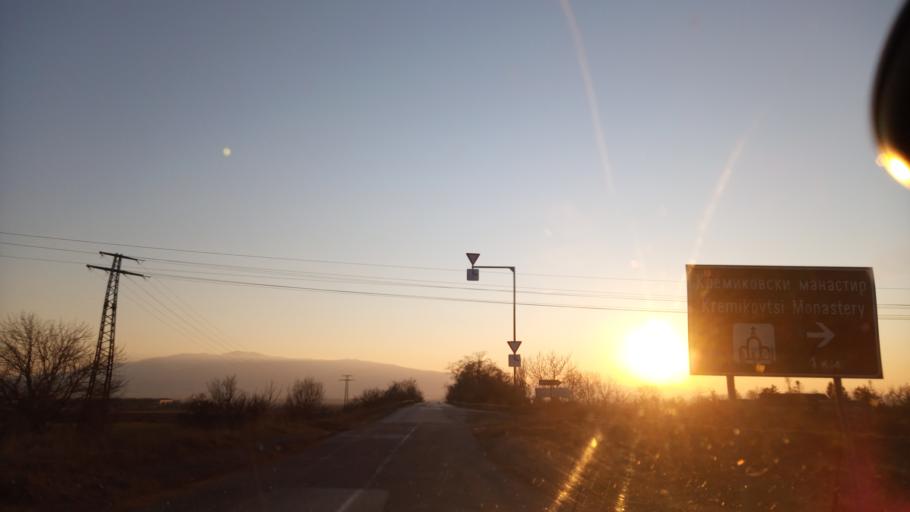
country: BG
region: Sofia-Capital
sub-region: Stolichna Obshtina
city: Bukhovo
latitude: 42.7705
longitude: 23.4980
